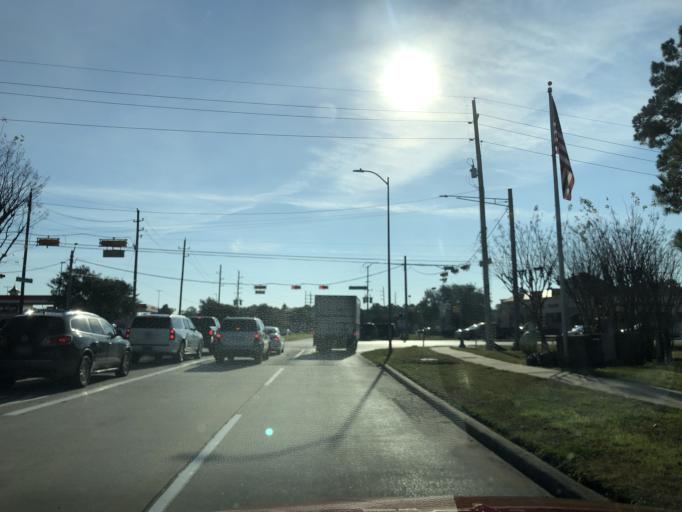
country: US
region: Texas
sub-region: Harris County
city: Tomball
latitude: 30.0334
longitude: -95.5559
